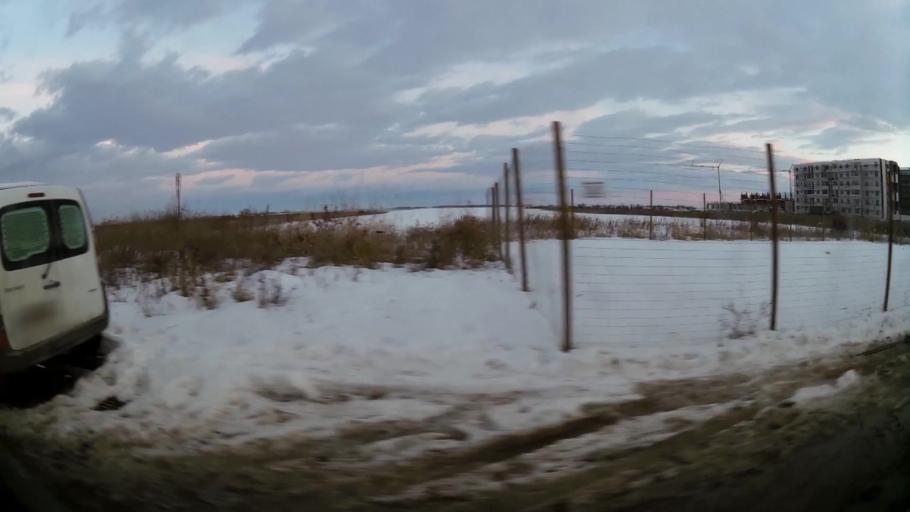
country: RO
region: Ilfov
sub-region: Comuna Popesti-Leordeni
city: Popesti-Leordeni
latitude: 44.3632
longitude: 26.1516
